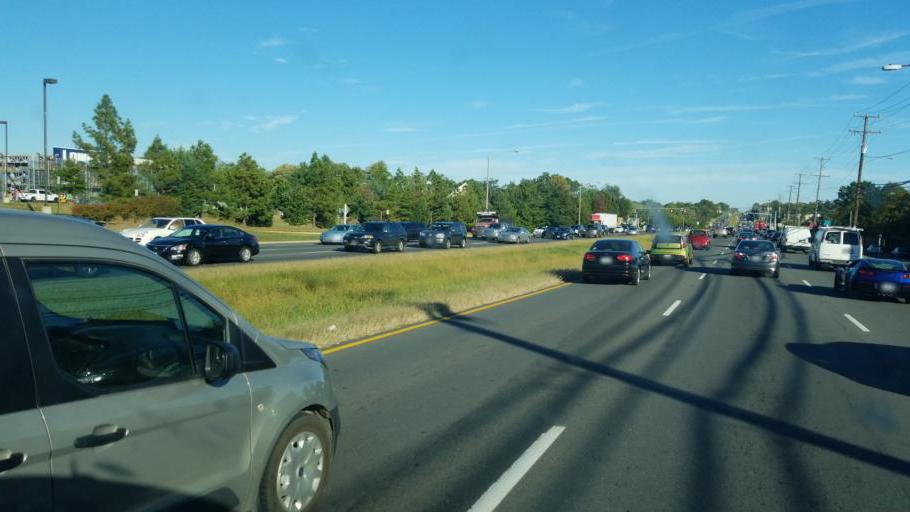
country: US
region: Virginia
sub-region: Fairfax County
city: Chantilly
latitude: 38.8917
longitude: -77.4251
